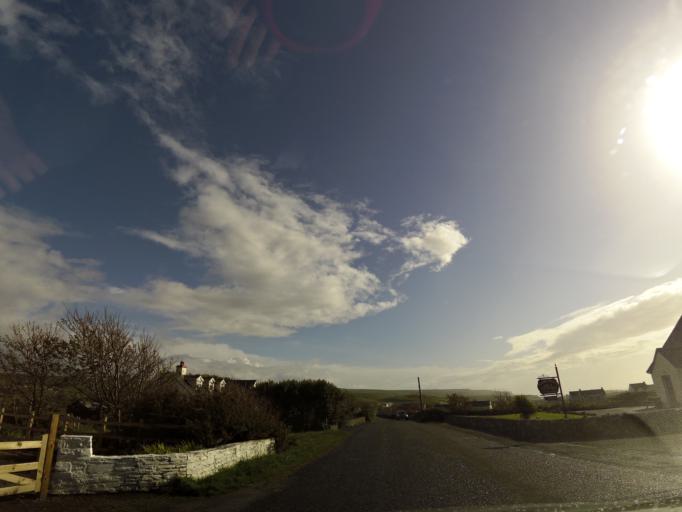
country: IE
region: Connaught
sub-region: County Galway
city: Bearna
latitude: 53.0218
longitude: -9.3693
